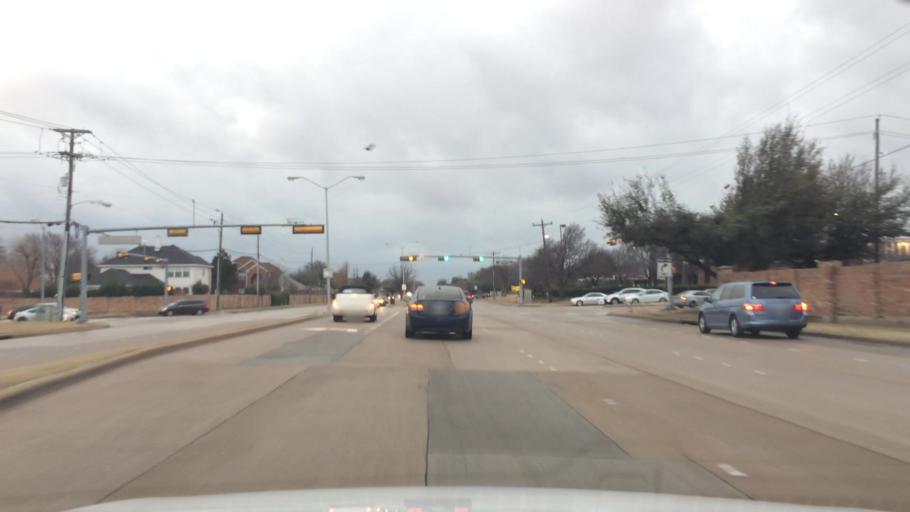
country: US
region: Texas
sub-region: Collin County
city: Frisco
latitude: 33.0867
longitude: -96.7717
